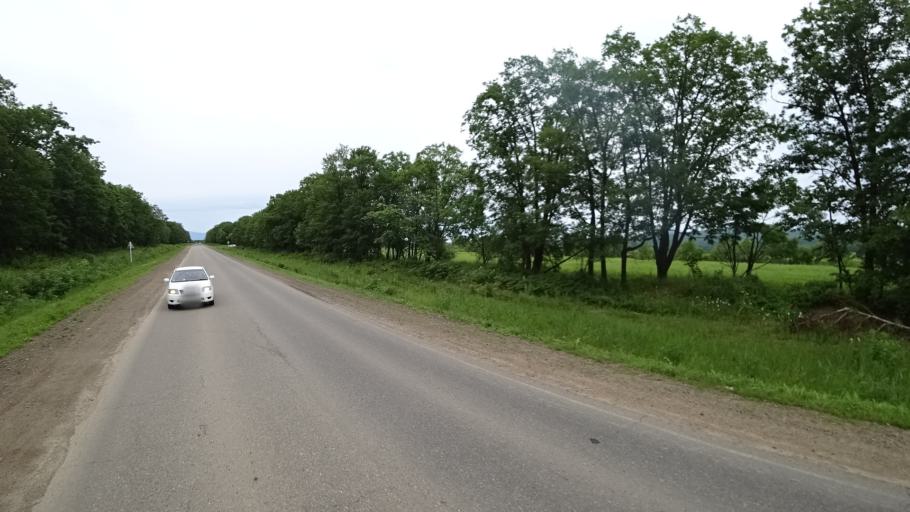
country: RU
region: Primorskiy
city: Novosysoyevka
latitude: 44.1897
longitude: 133.3546
